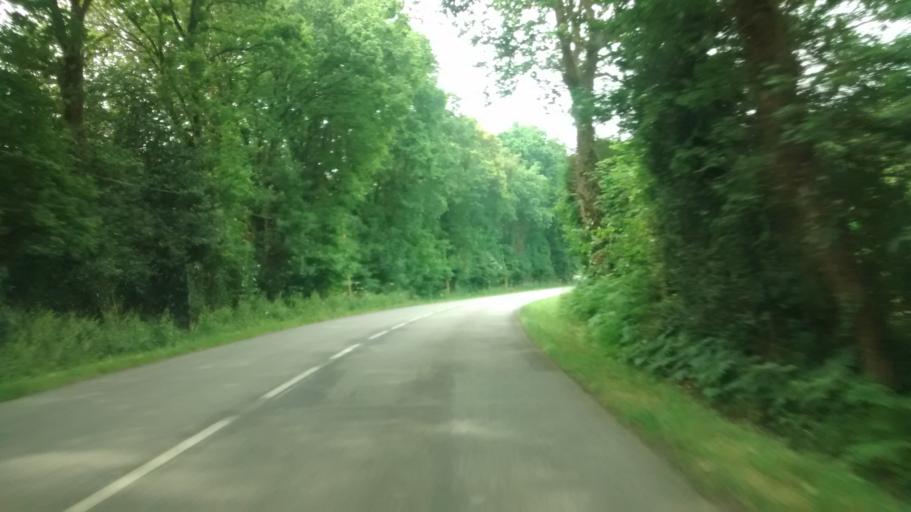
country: FR
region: Brittany
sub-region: Departement du Morbihan
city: Caro
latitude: 47.8392
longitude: -2.3071
